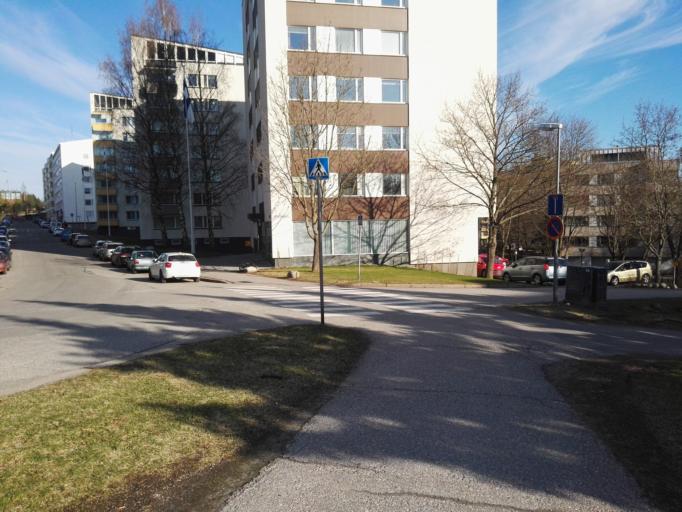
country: FI
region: Paijanne Tavastia
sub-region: Lahti
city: Lahti
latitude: 60.9796
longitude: 25.6614
